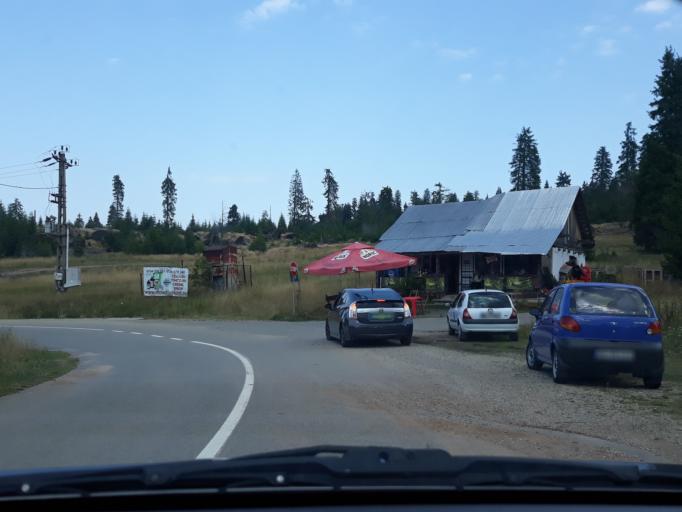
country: RO
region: Alba
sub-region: Comuna Arieseni
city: Arieseni
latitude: 46.5976
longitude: 22.7328
